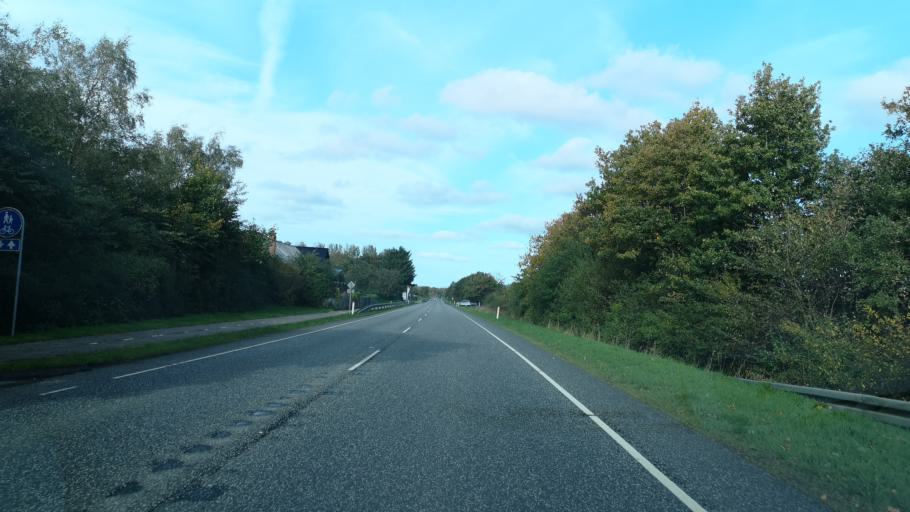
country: DK
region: Central Jutland
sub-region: Holstebro Kommune
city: Holstebro
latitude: 56.3281
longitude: 8.6107
